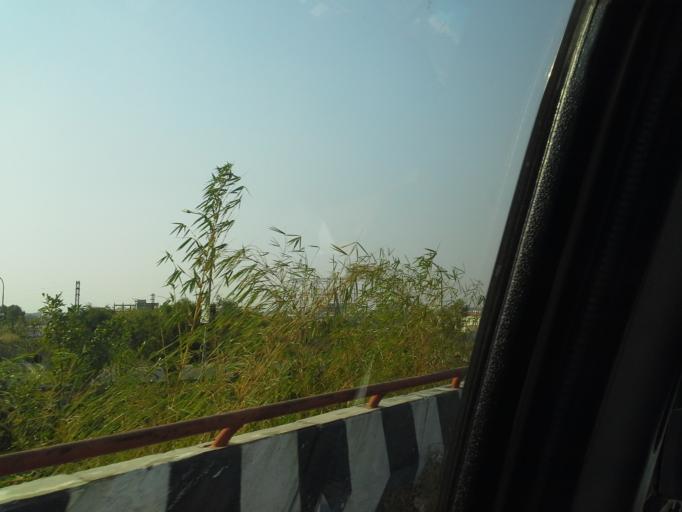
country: IN
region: Telangana
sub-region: Rangareddi
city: Sriramnagar
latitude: 17.2536
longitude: 78.3822
